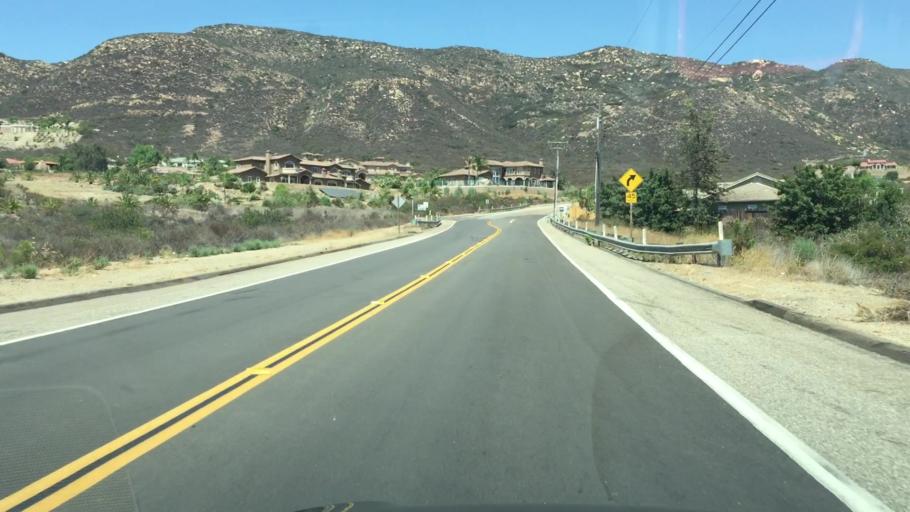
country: US
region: California
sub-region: San Diego County
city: Jamul
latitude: 32.7338
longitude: -116.8515
